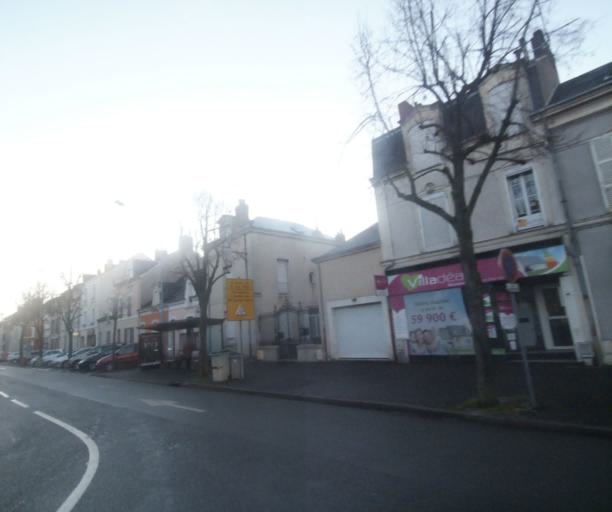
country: FR
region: Pays de la Loire
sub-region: Departement de la Sarthe
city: Le Mans
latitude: 48.0011
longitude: 0.1840
